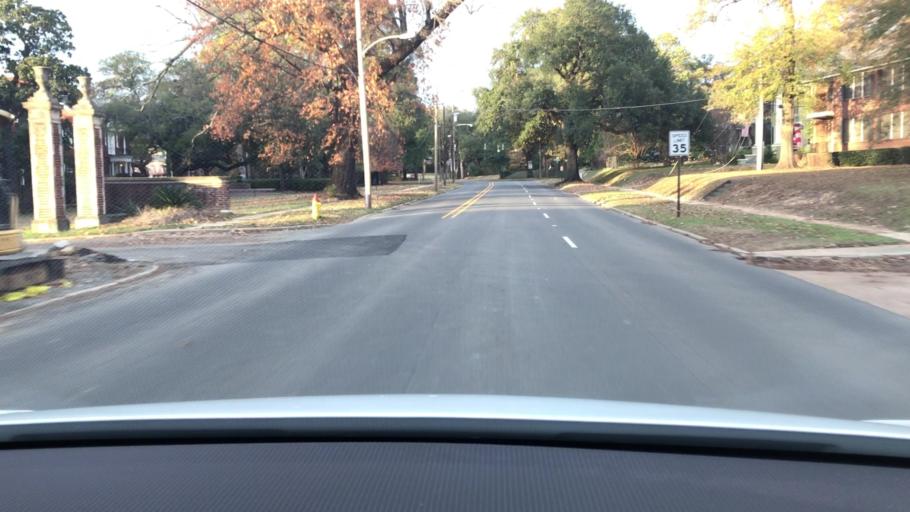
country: US
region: Louisiana
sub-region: Bossier Parish
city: Bossier City
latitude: 32.4843
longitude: -93.7498
